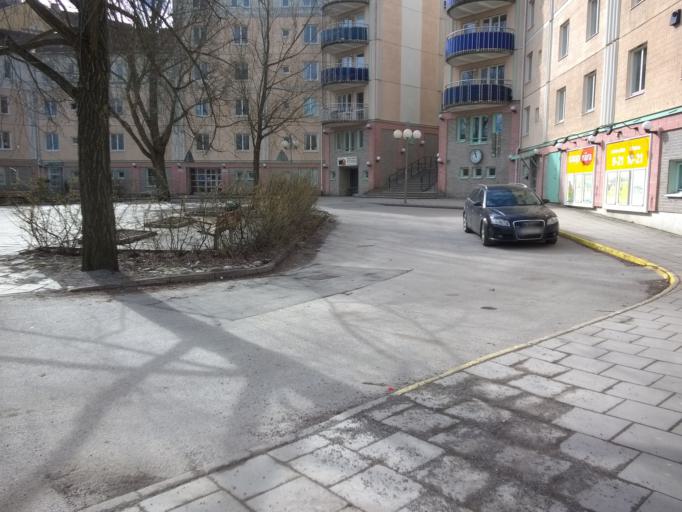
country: SE
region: Stockholm
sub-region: Solna Kommun
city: Solna
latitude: 59.3394
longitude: 17.9896
